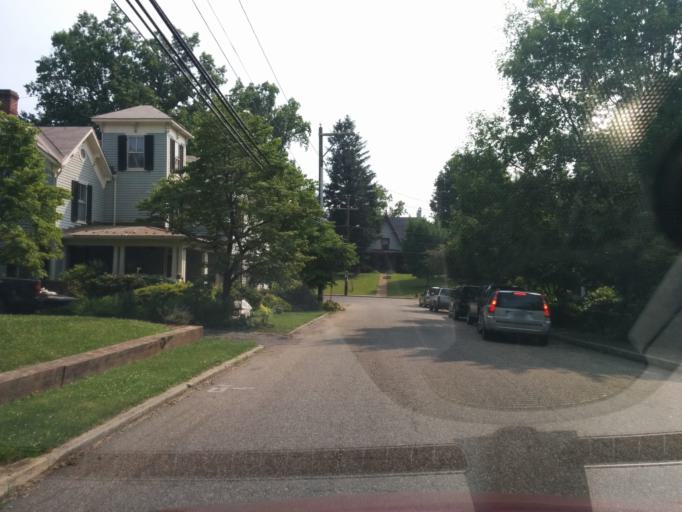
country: US
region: Virginia
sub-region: City of Lexington
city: Lexington
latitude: 37.7820
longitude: -79.4468
